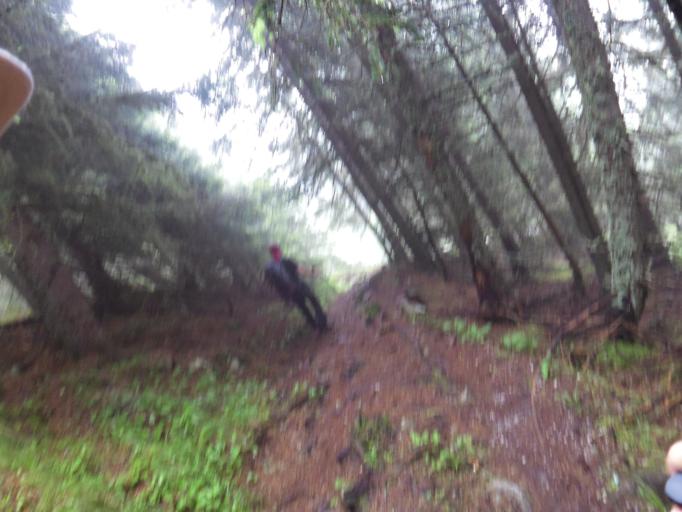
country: AT
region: Tyrol
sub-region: Politischer Bezirk Innsbruck Land
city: Neustift im Stubaital
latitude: 47.0515
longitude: 11.2245
